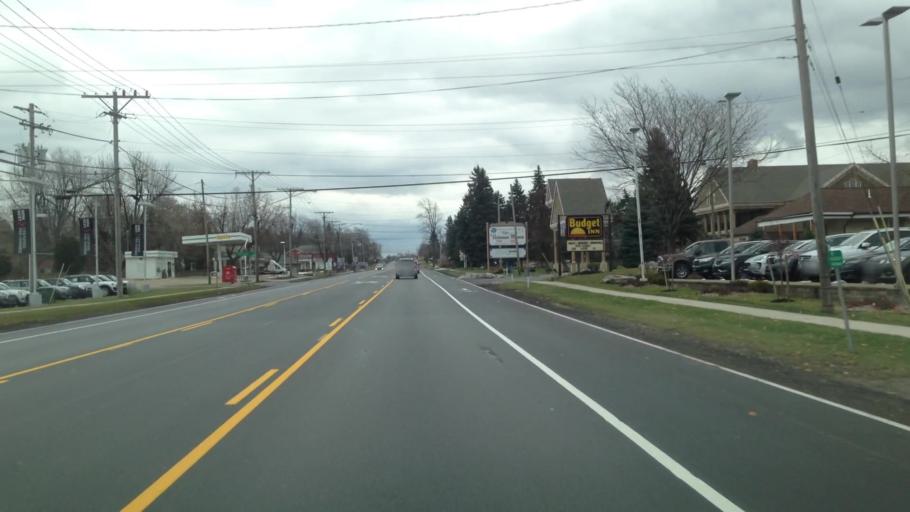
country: US
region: New York
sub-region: Erie County
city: Harris Hill
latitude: 42.9650
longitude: -78.6879
